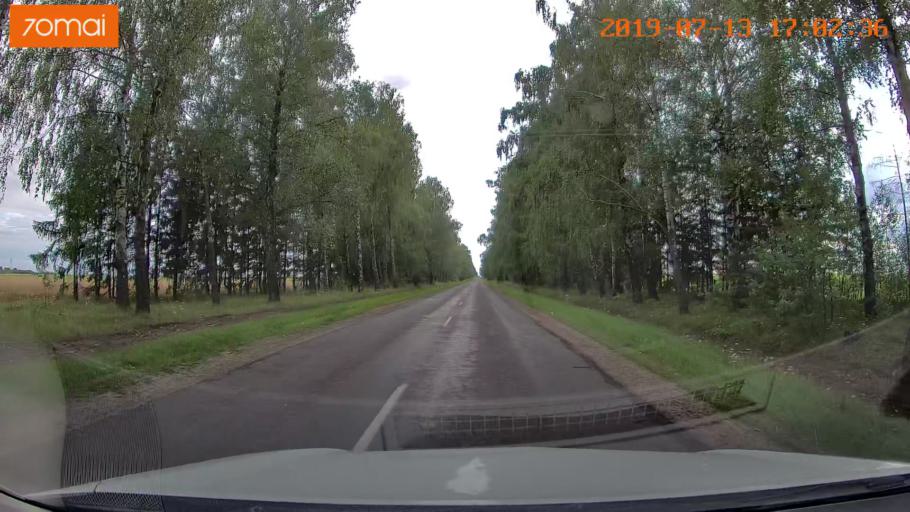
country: BY
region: Mogilev
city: Kirawsk
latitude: 53.2843
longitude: 29.3853
